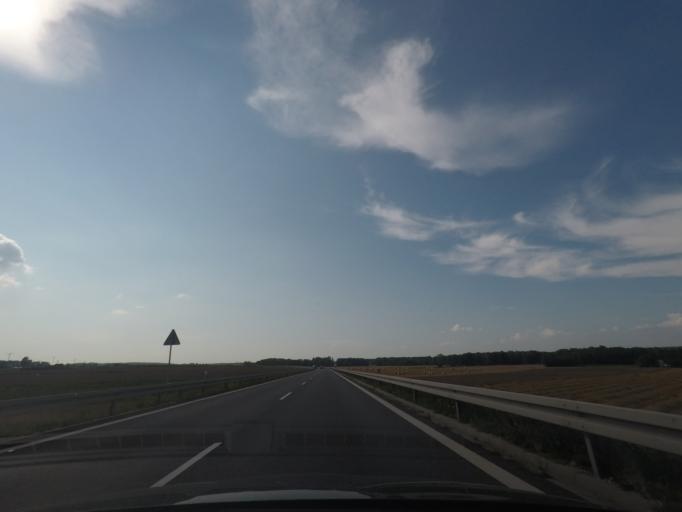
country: PL
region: Silesian Voivodeship
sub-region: Powiat pszczynski
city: Piasek
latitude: 49.9993
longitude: 18.9385
